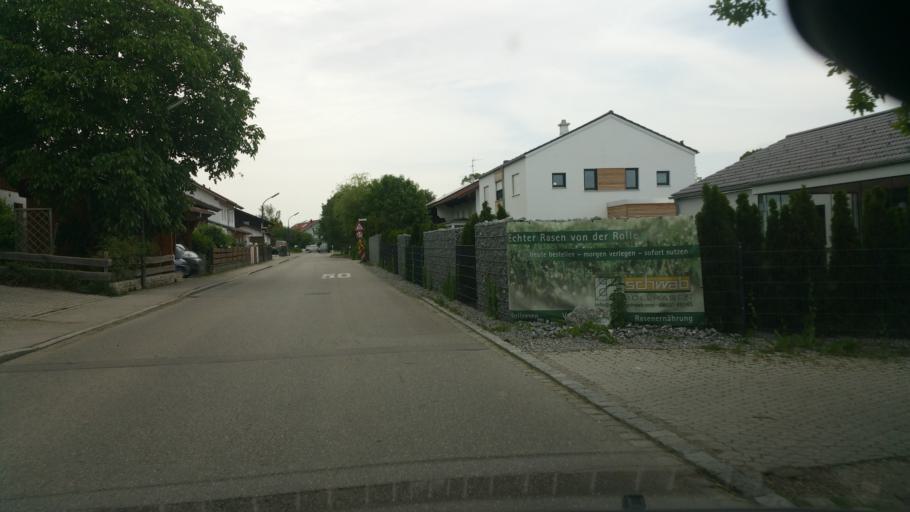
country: DE
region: Bavaria
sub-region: Upper Bavaria
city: Bruckmuhl
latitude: 47.8698
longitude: 11.9108
